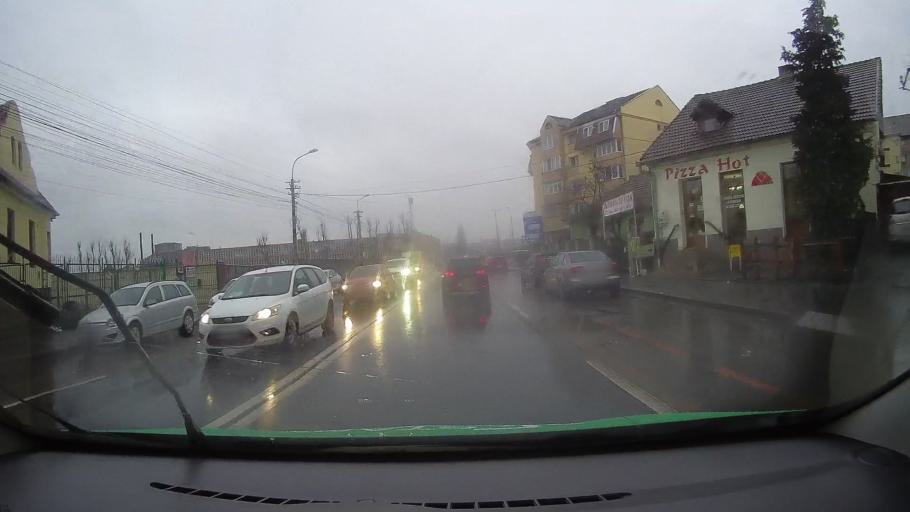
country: RO
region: Sibiu
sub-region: Municipiul Sibiu
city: Sibiu
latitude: 45.8063
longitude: 24.1518
